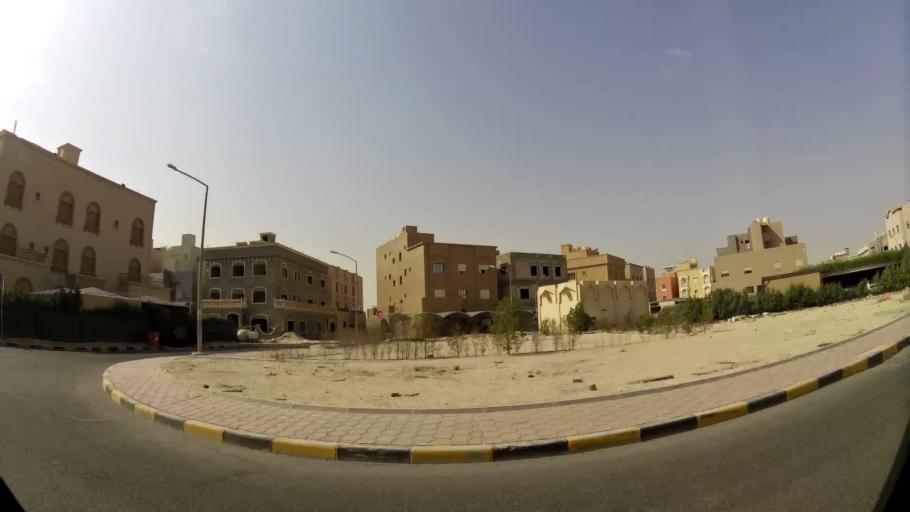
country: KW
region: Muhafazat al Jahra'
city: Al Jahra'
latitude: 29.3393
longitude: 47.7676
